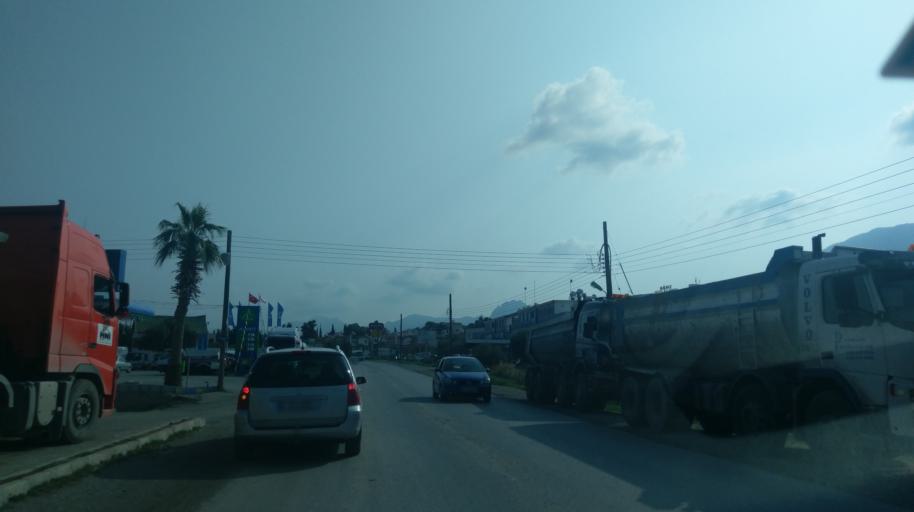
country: CY
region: Keryneia
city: Kyrenia
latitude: 35.3252
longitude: 33.3982
